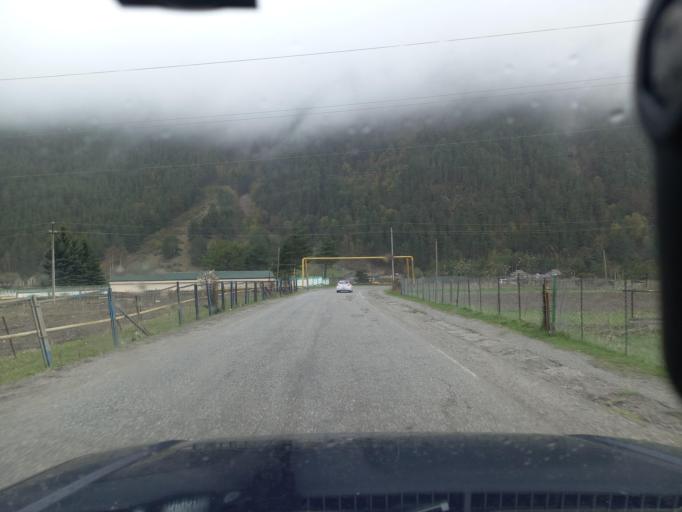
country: RU
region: Kabardino-Balkariya
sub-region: El'brusskiy Rayon
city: El'brus
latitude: 43.2579
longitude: 42.6470
